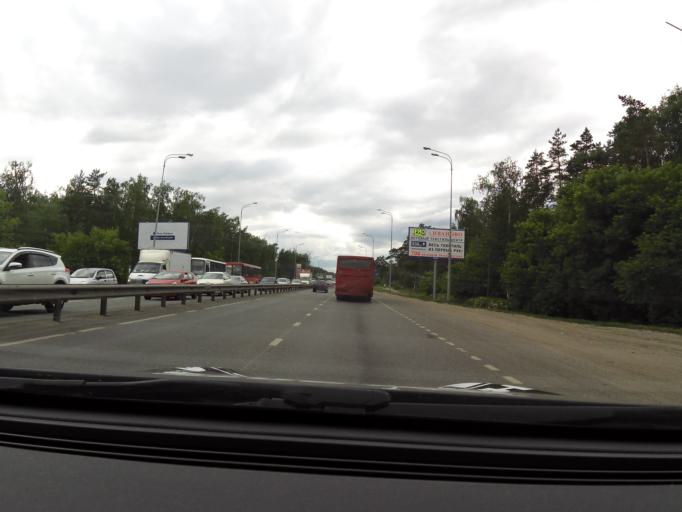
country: RU
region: Tatarstan
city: Staroye Arakchino
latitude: 55.8277
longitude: 49.0183
